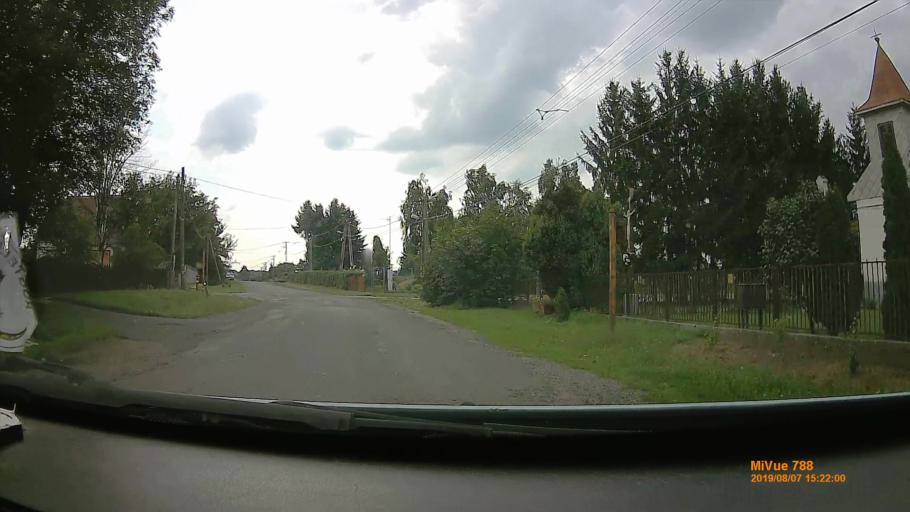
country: HU
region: Borsod-Abauj-Zemplen
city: Encs
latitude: 48.3610
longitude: 21.1480
